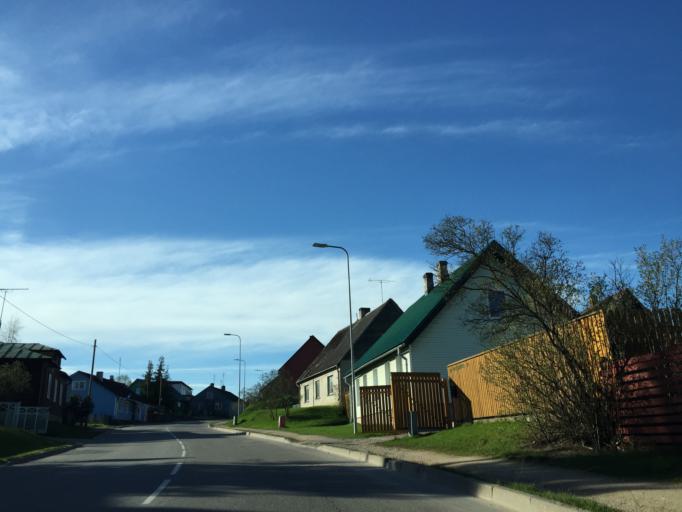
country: EE
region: Valgamaa
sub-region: Valga linn
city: Valga
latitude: 57.7820
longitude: 26.0287
